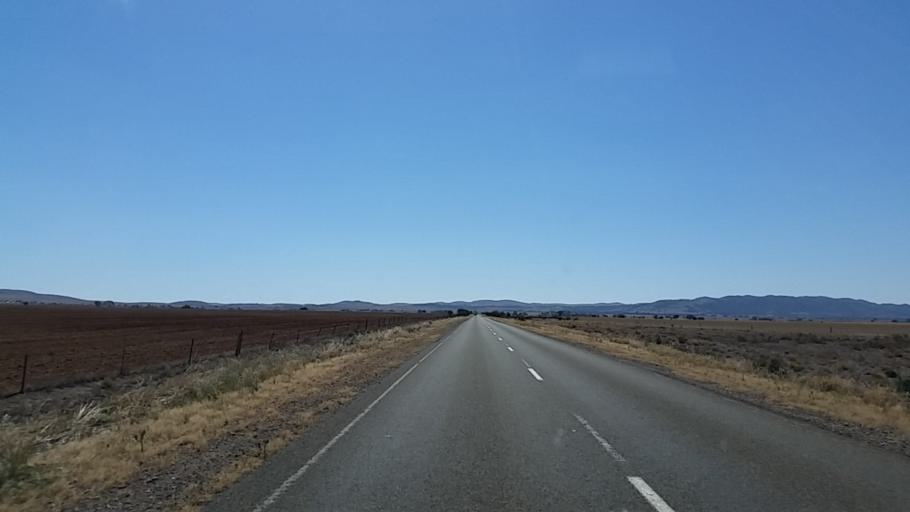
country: AU
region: South Australia
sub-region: Peterborough
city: Peterborough
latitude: -32.6596
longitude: 138.6048
